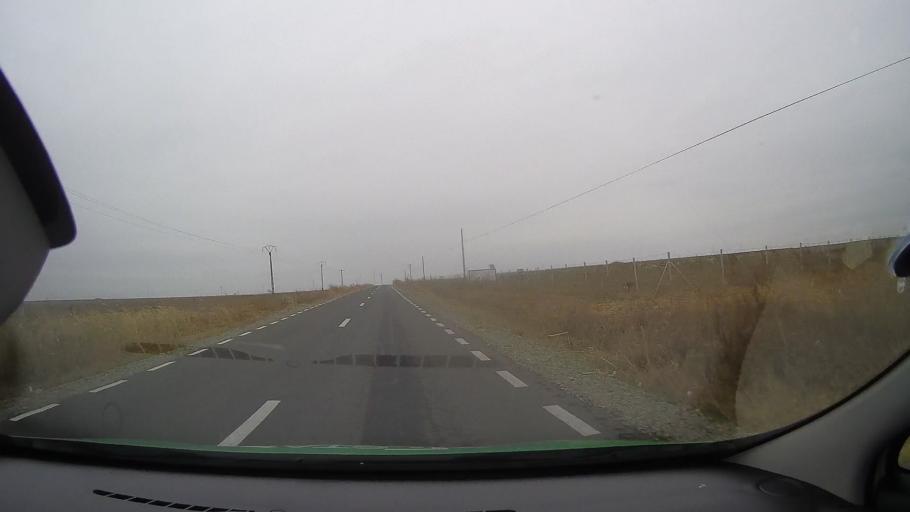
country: RO
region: Constanta
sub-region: Comuna Tortoman
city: Tortoman
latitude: 44.3548
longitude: 28.2134
